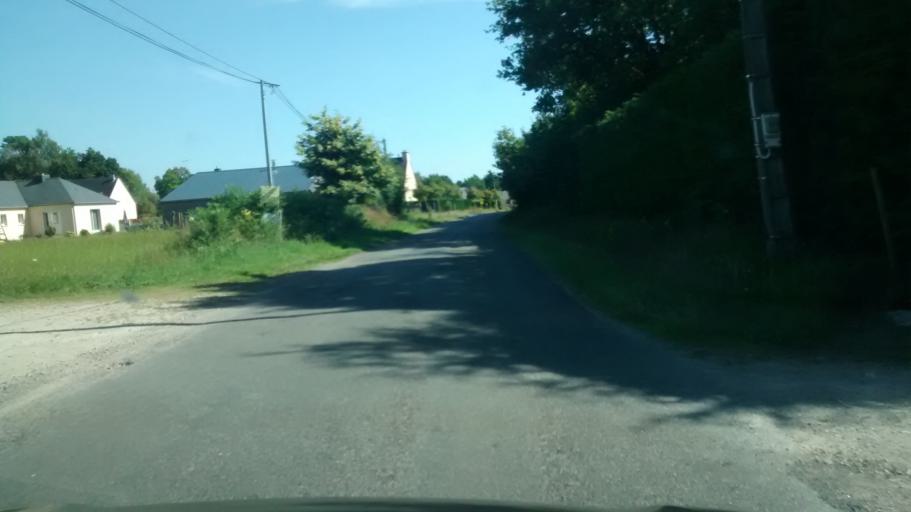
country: FR
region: Brittany
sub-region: Departement du Morbihan
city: Molac
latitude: 47.7396
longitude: -2.4358
